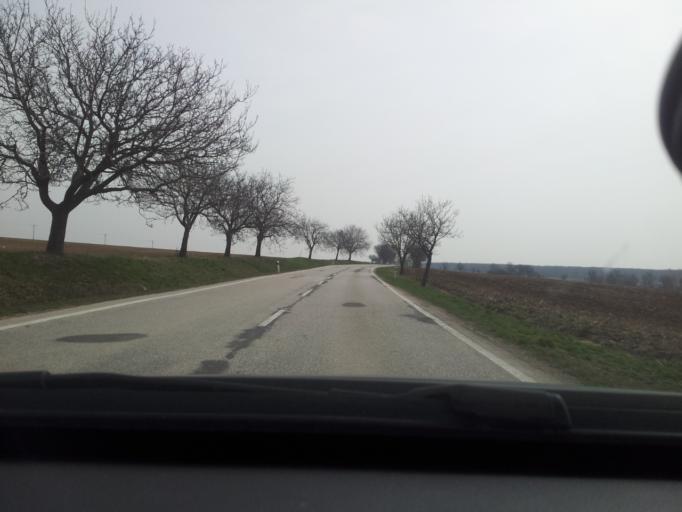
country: SK
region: Nitriansky
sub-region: Okres Nitra
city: Nitra
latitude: 48.3459
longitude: 17.9630
